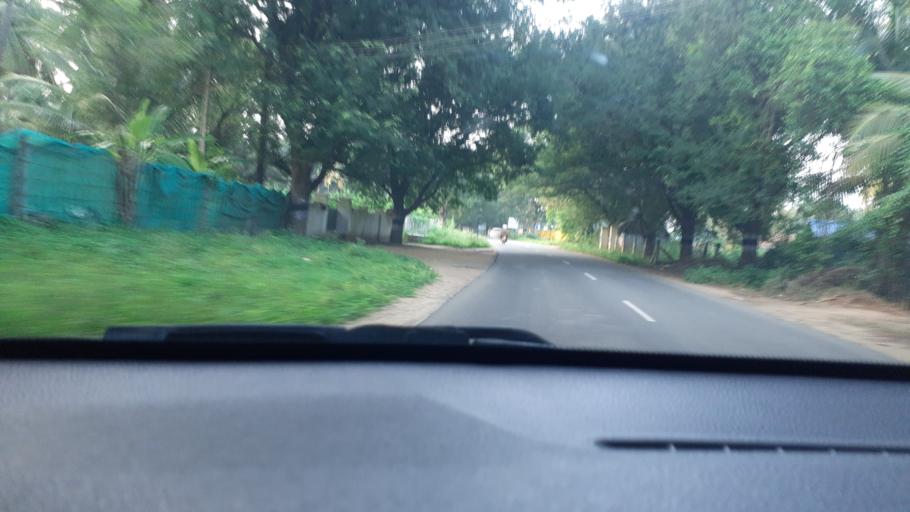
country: IN
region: Tamil Nadu
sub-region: Dindigul
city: Palani
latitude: 10.4216
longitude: 77.5345
